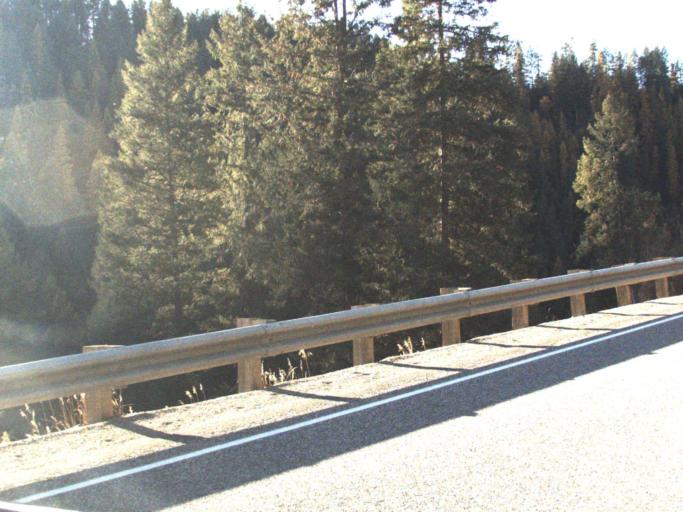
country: CA
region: British Columbia
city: Rossland
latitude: 48.9451
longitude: -117.7914
